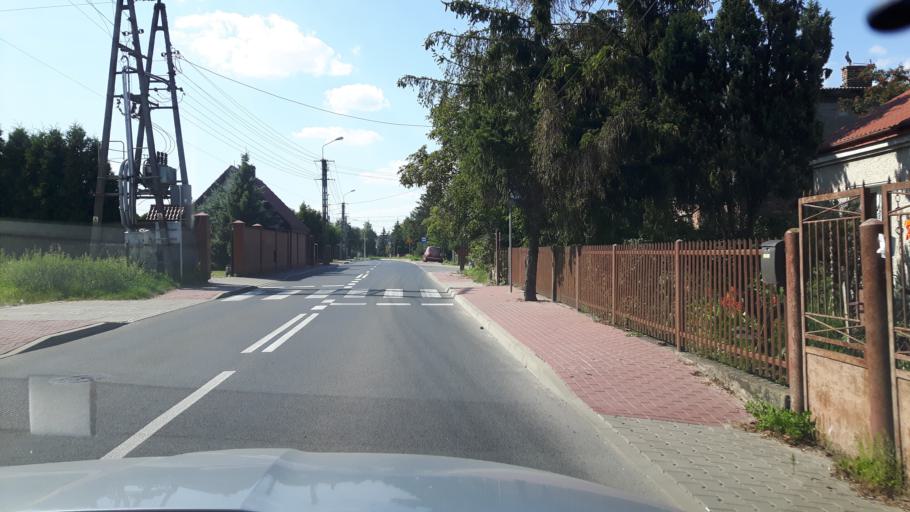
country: PL
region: Masovian Voivodeship
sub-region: Powiat pruszkowski
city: Nowe Grocholice
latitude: 52.1679
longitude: 20.9060
